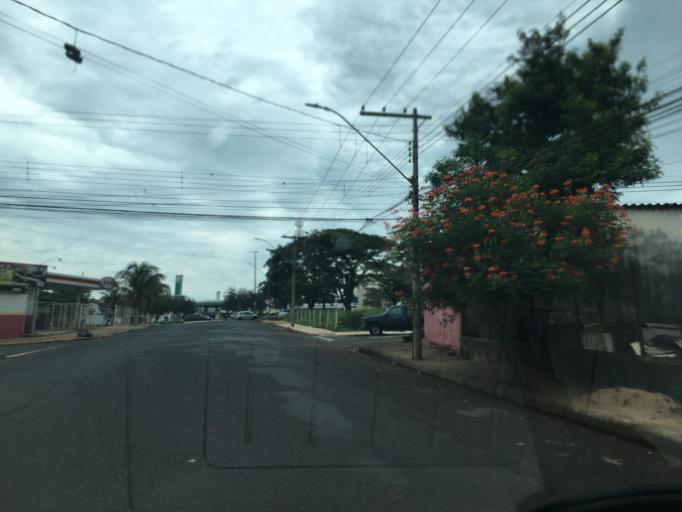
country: BR
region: Minas Gerais
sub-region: Uberlandia
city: Uberlandia
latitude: -18.9120
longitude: -48.3040
